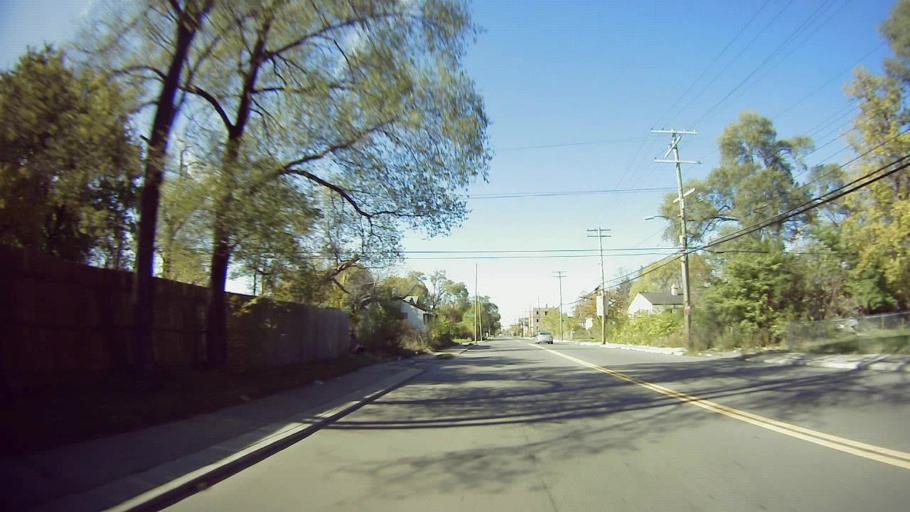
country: US
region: Michigan
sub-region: Wayne County
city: Dearborn
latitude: 42.3883
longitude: -83.1659
